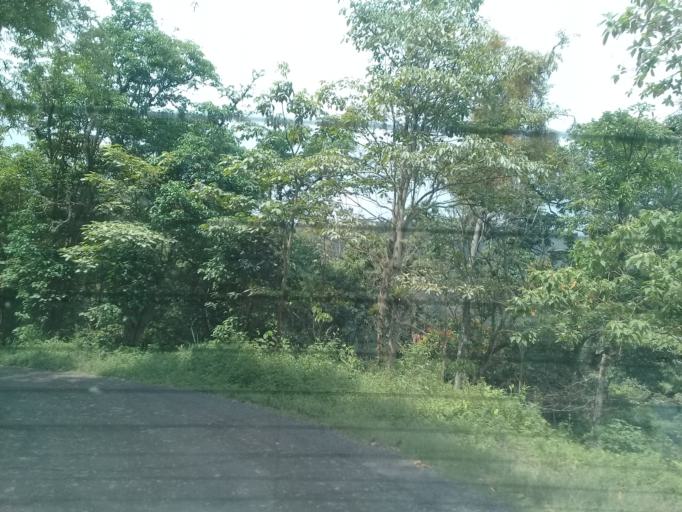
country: CO
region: Cundinamarca
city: Quipile
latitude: 4.7116
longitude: -74.5464
